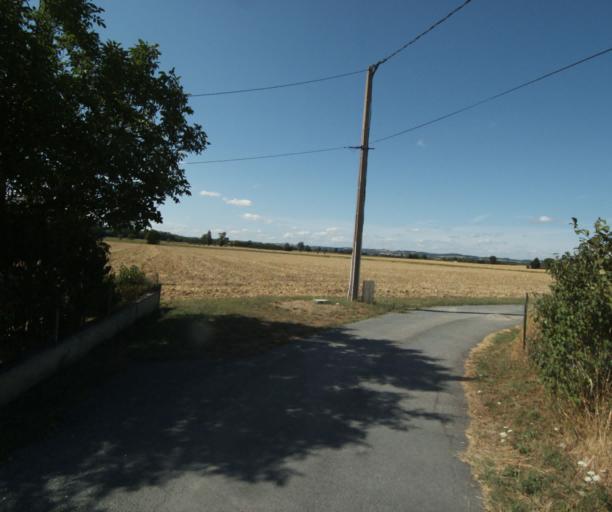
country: FR
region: Midi-Pyrenees
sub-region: Departement de la Haute-Garonne
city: Revel
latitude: 43.4999
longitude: 1.9722
